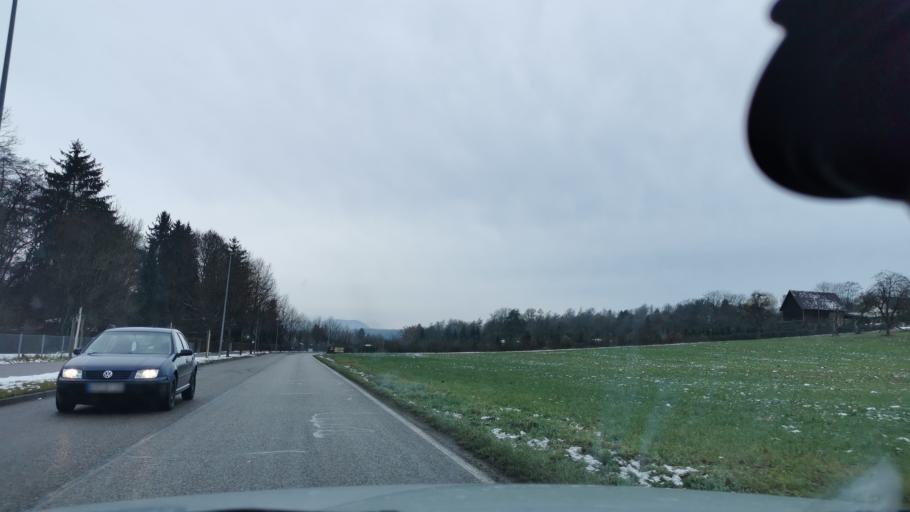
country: DE
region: Baden-Wuerttemberg
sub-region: Regierungsbezirk Stuttgart
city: Eislingen
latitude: 48.7104
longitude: 9.6826
